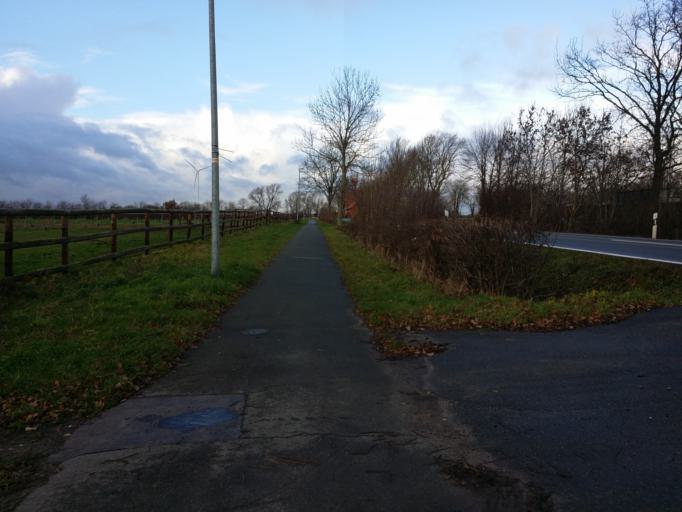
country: DE
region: Lower Saxony
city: Riede
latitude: 52.9943
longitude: 8.9220
